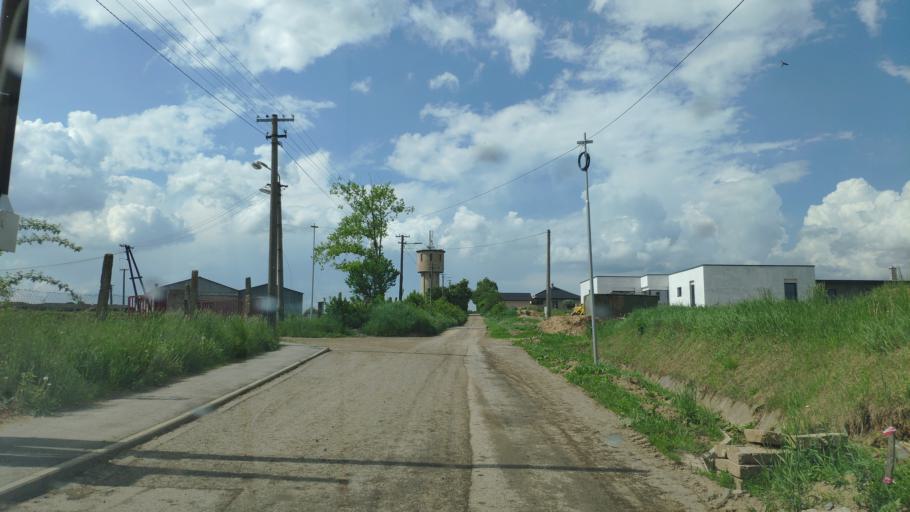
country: SK
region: Presovsky
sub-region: Okres Presov
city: Presov
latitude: 49.0162
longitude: 21.1851
